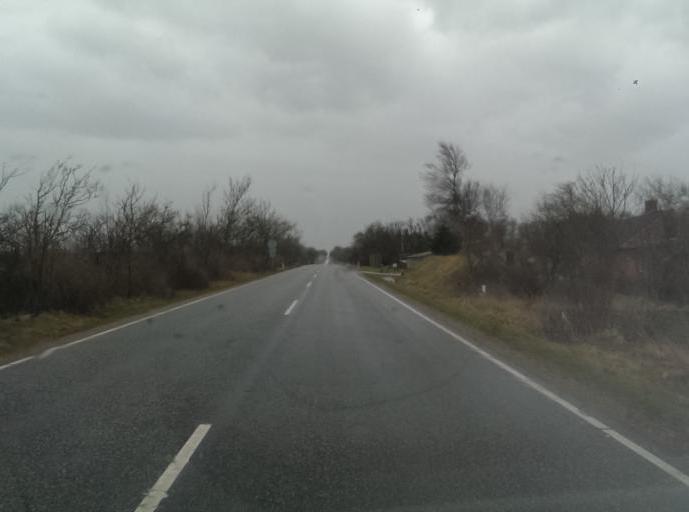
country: DK
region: Central Jutland
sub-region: Ringkobing-Skjern Kommune
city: Ringkobing
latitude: 56.0828
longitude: 8.3996
